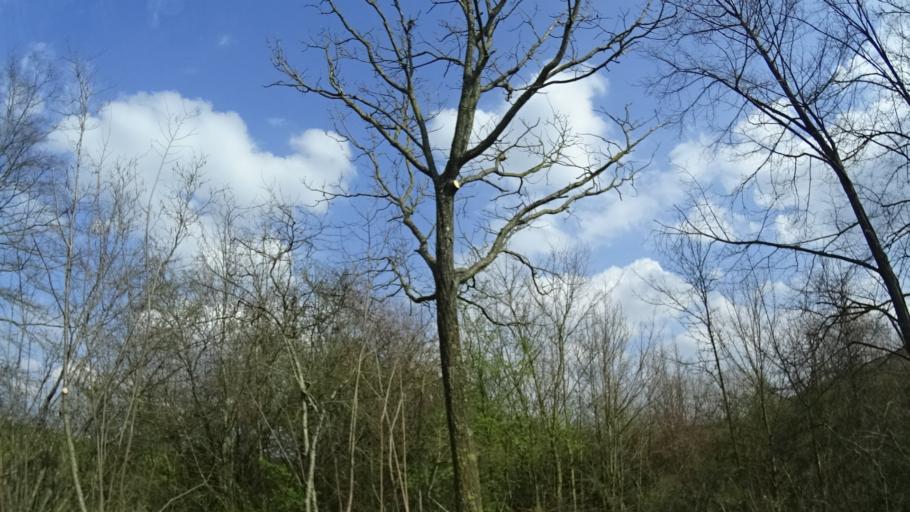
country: DE
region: Bavaria
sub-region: Regierungsbezirk Unterfranken
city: Castell
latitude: 49.7726
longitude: 10.3788
